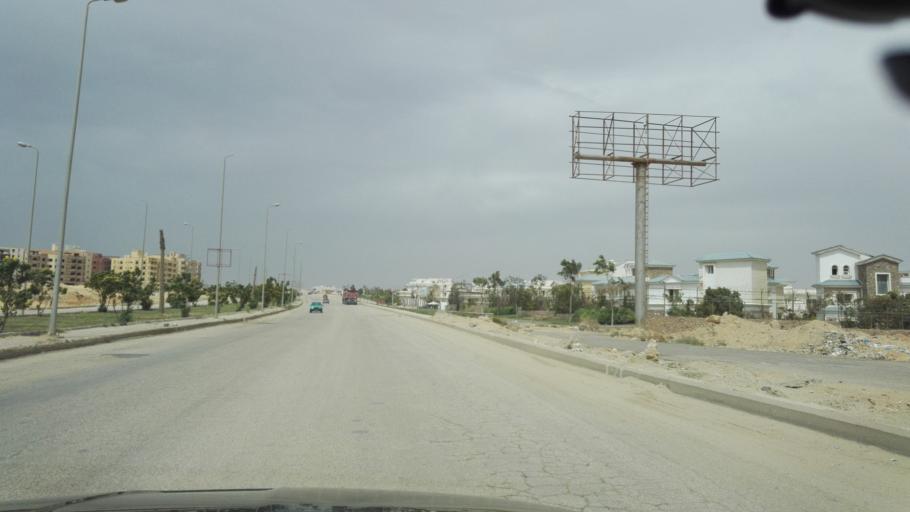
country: EG
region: Muhafazat al Qalyubiyah
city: Al Khankah
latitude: 30.0302
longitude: 31.5290
